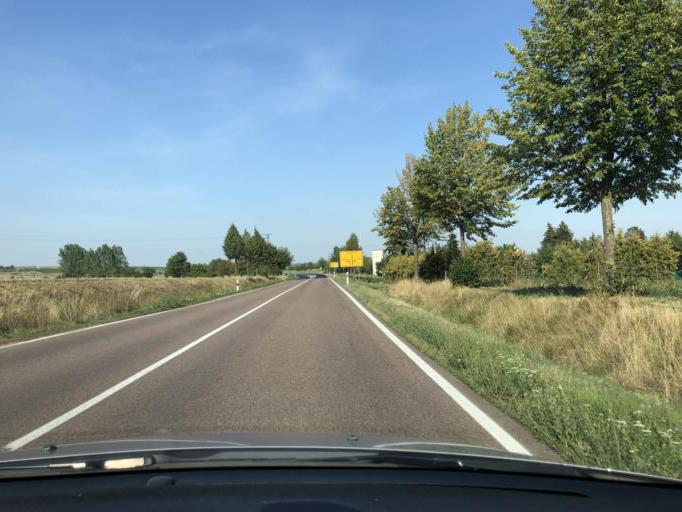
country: DE
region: Saxony-Anhalt
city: Goseck
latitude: 51.2378
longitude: 11.8256
